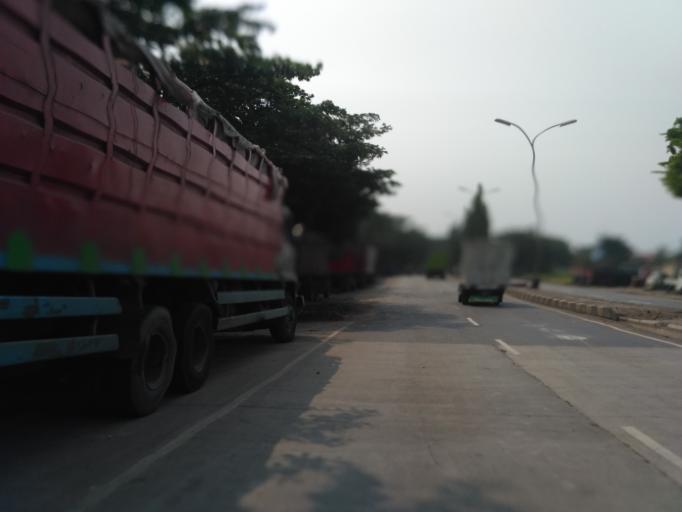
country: ID
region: Central Java
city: Semarang
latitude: -6.9768
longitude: 110.3875
